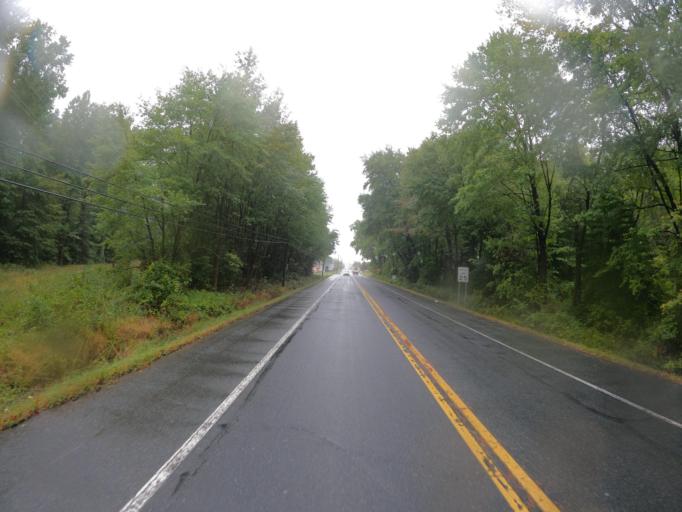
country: US
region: Delaware
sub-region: Sussex County
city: Milford
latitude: 38.8071
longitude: -75.4175
